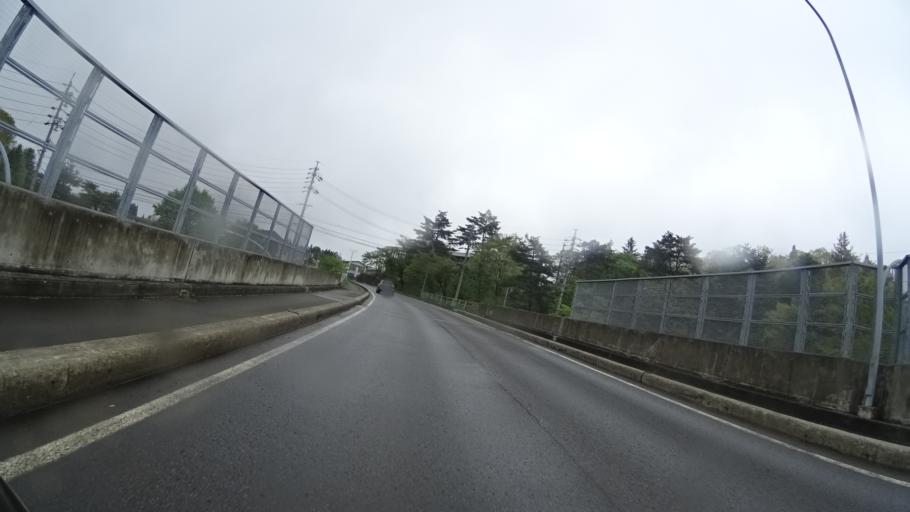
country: JP
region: Nagano
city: Nagano-shi
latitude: 36.8080
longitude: 138.2000
